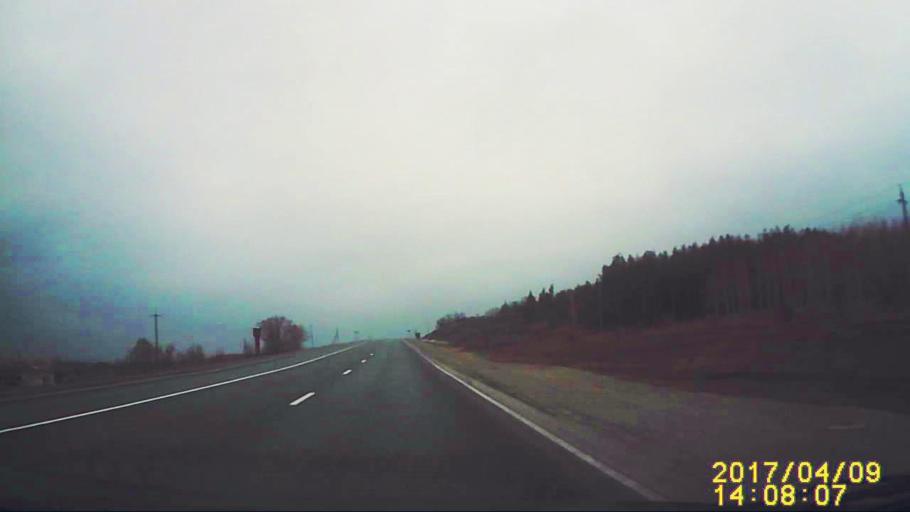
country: RU
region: Ulyanovsk
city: Silikatnyy
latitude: 54.0176
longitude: 48.2163
